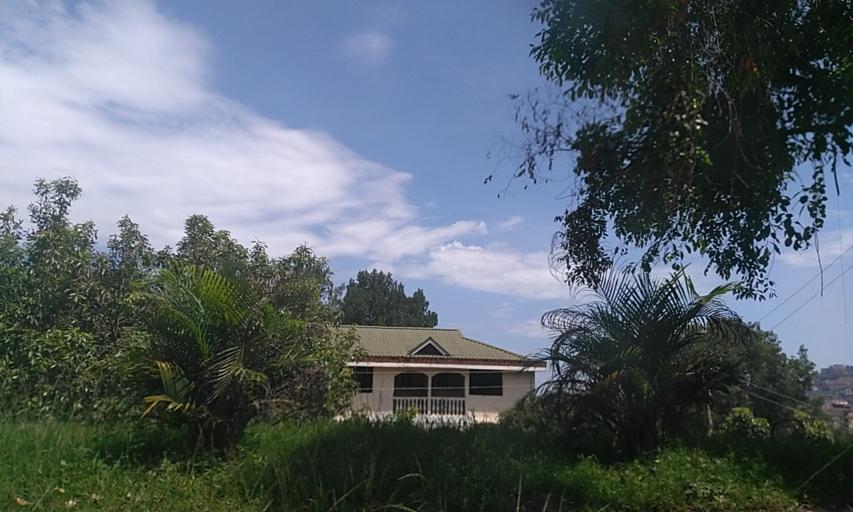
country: UG
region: Central Region
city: Kampala Central Division
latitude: 0.3377
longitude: 32.5906
